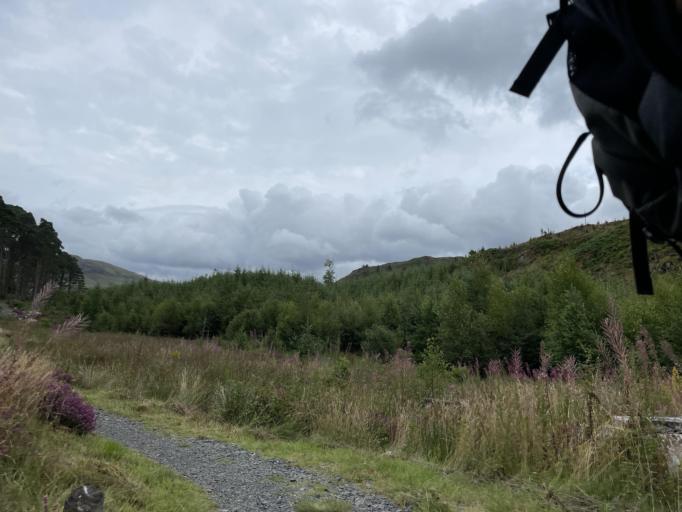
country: GB
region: Scotland
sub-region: Dumfries and Galloway
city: Newton Stewart
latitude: 55.0818
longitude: -4.4993
